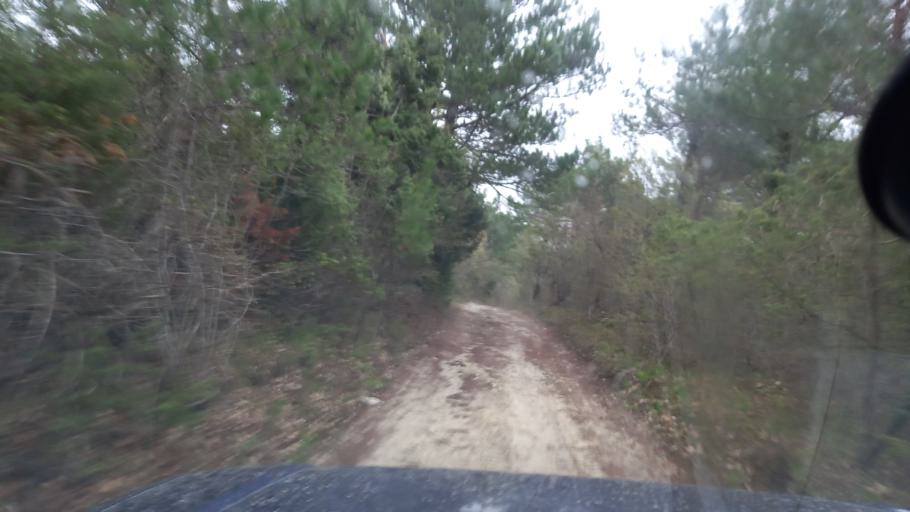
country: RU
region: Krasnodarskiy
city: Dzhubga
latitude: 44.3194
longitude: 38.6693
